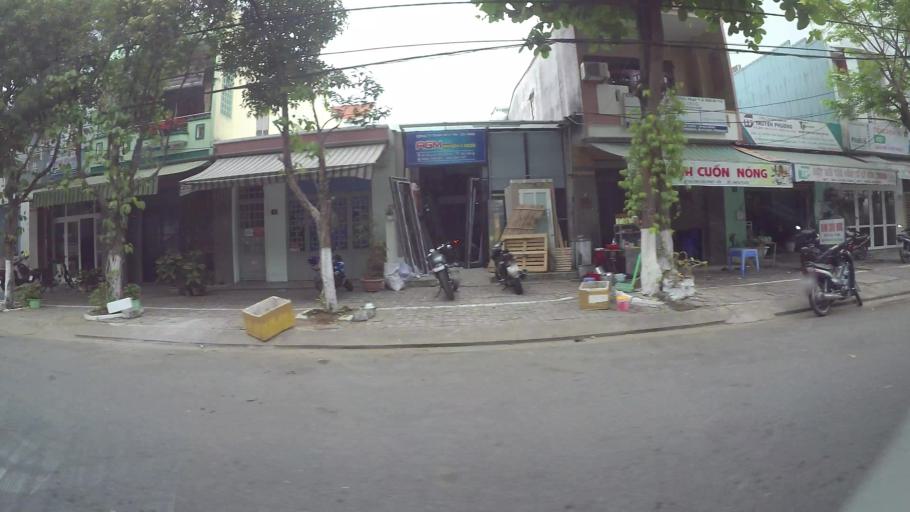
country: VN
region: Da Nang
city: Cam Le
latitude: 16.0372
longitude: 108.2141
